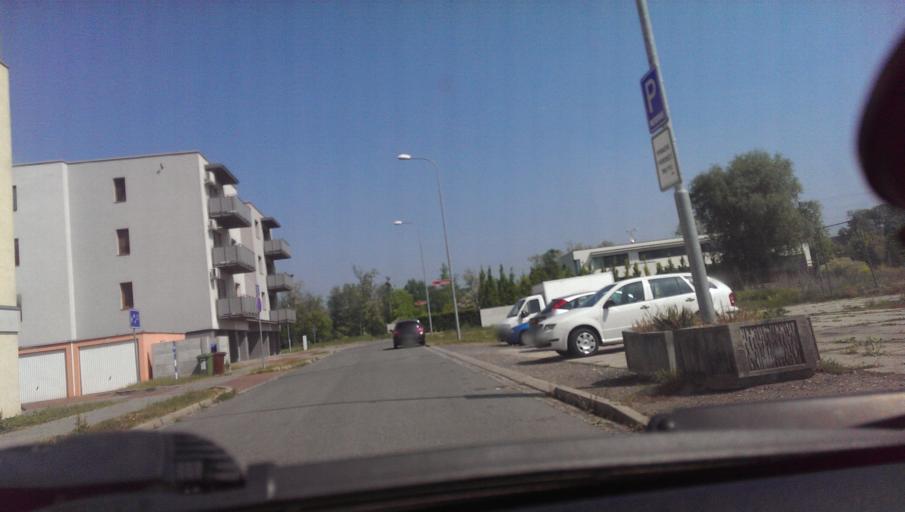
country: CZ
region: Zlin
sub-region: Okres Uherske Hradiste
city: Uherske Hradiste
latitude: 49.0719
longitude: 17.4732
